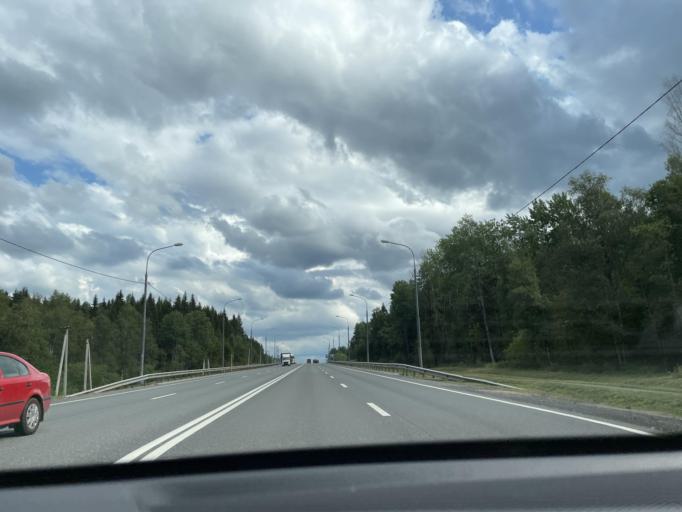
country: RU
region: Novgorod
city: Valday
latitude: 57.9969
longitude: 33.1663
